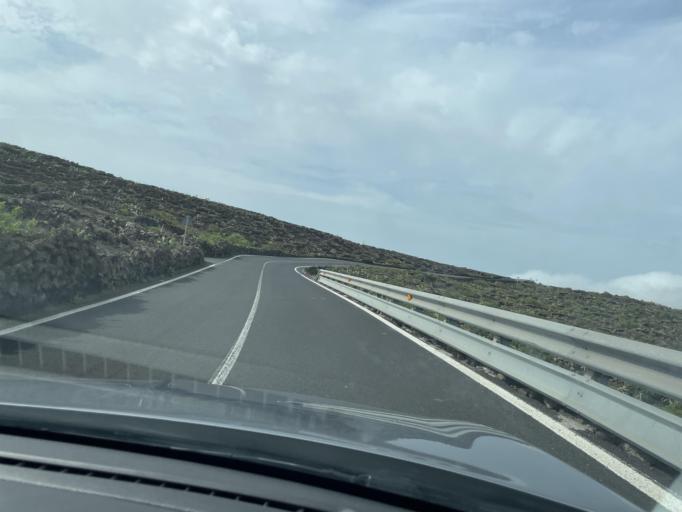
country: ES
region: Canary Islands
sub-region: Provincia de Las Palmas
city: Haria
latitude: 29.1914
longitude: -13.4725
